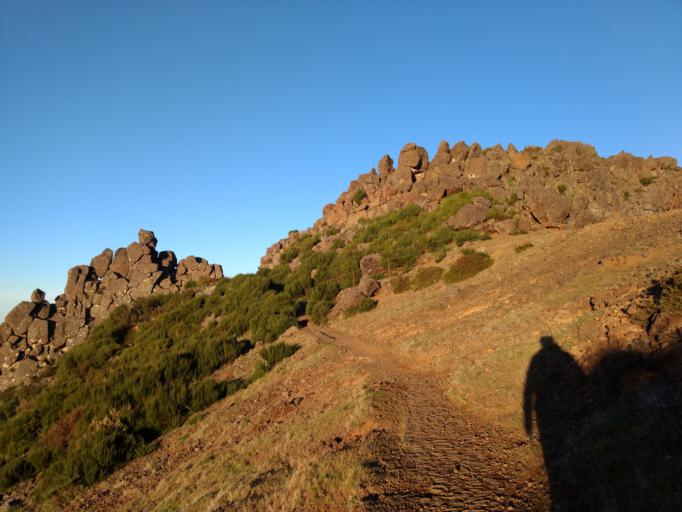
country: PT
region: Madeira
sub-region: Camara de Lobos
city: Curral das Freiras
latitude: 32.7361
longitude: -16.9262
